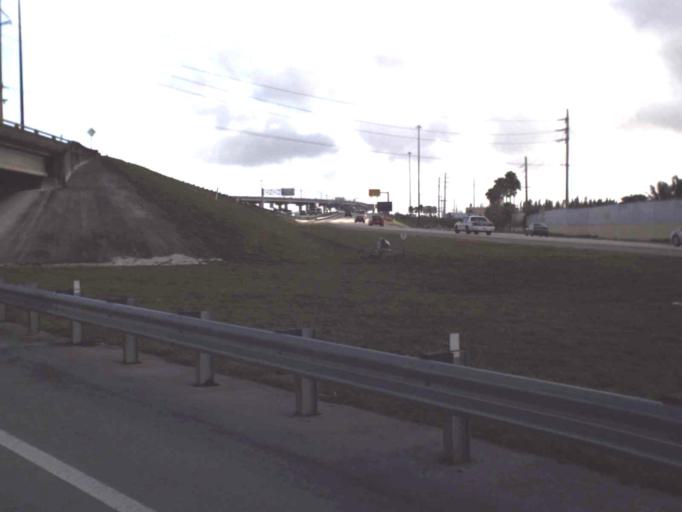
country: US
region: Florida
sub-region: Miami-Dade County
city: Norland
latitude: 25.9320
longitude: -80.2128
